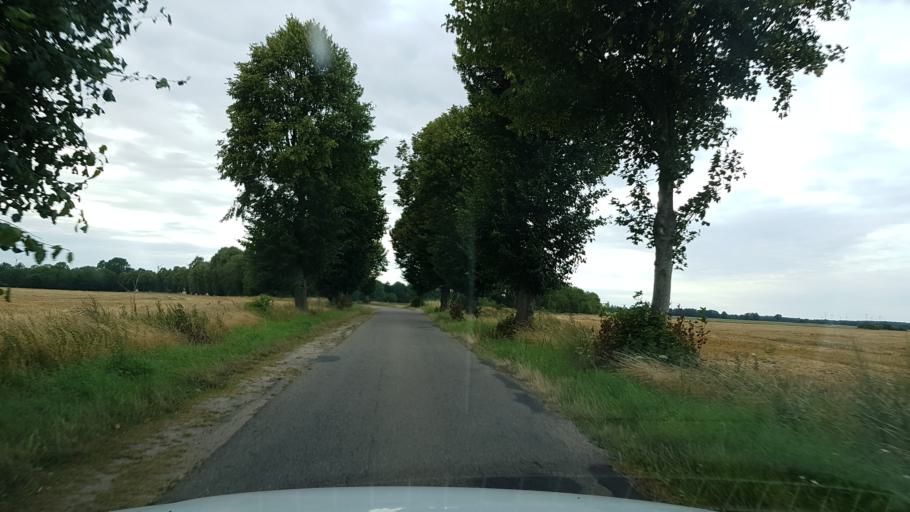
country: PL
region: West Pomeranian Voivodeship
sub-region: Powiat bialogardzki
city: Karlino
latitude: 54.1149
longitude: 15.8746
